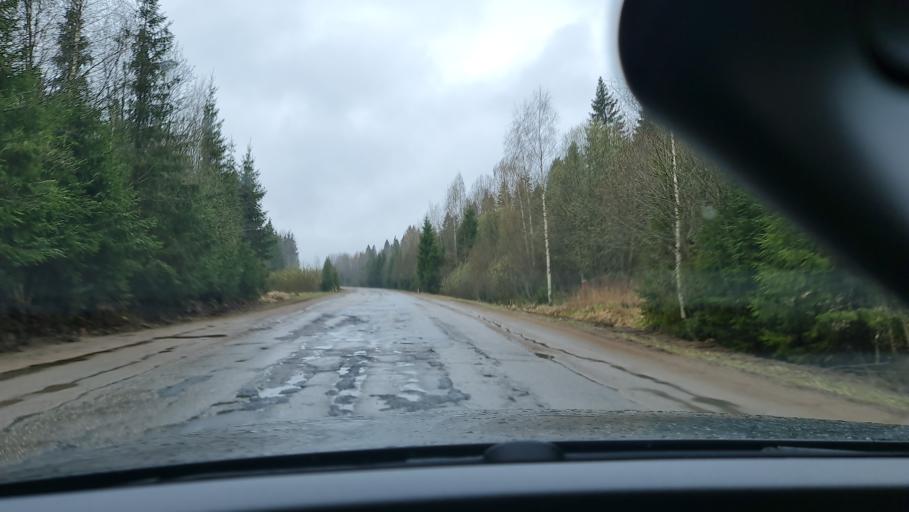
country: RU
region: Novgorod
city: Kresttsy
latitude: 58.0332
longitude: 32.8239
